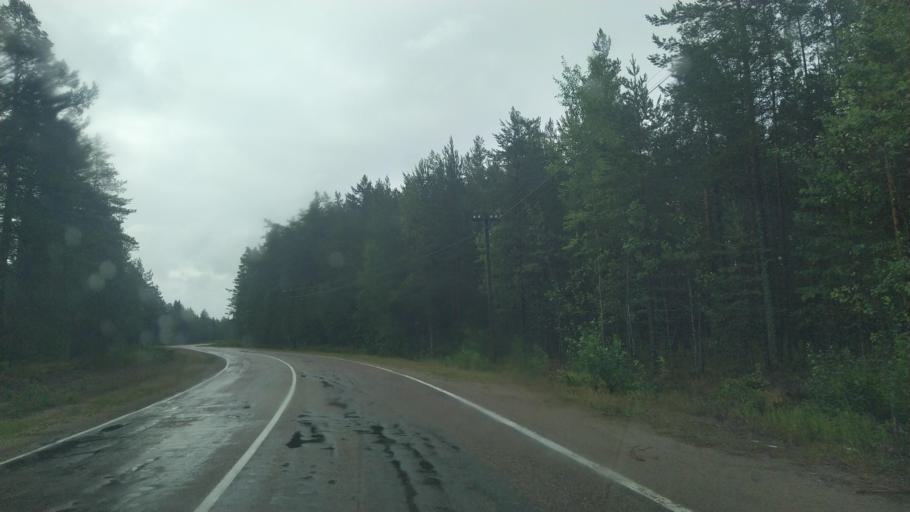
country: RU
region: Leningrad
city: Priozersk
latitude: 60.9796
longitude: 30.2709
